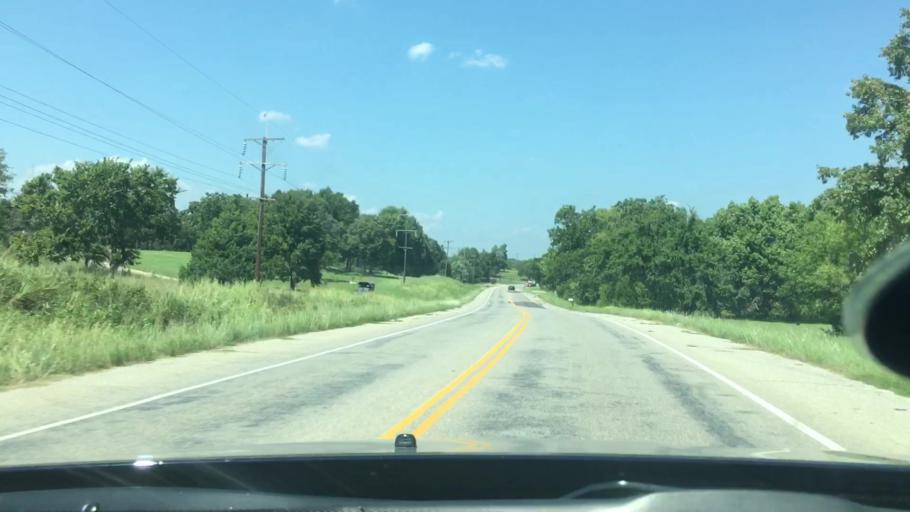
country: US
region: Oklahoma
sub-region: Pontotoc County
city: Byng
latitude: 34.8309
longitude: -96.6786
